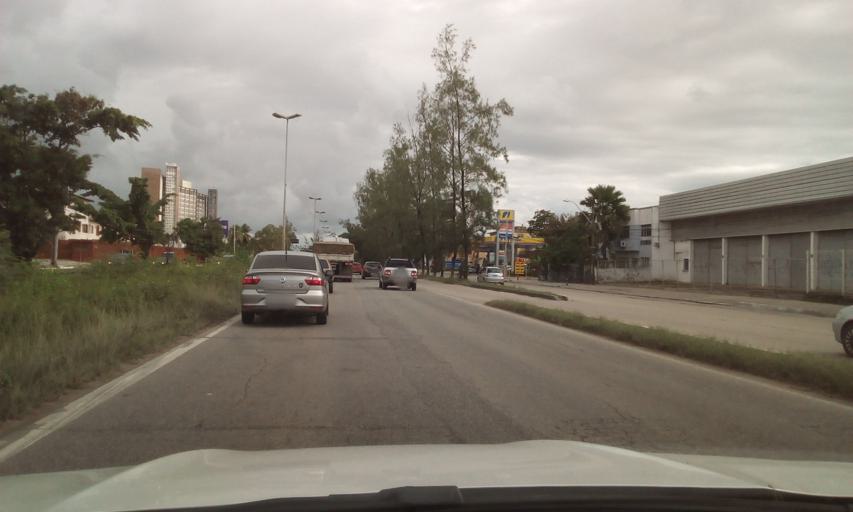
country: BR
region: Pernambuco
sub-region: Recife
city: Recife
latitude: -8.0435
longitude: -34.9437
